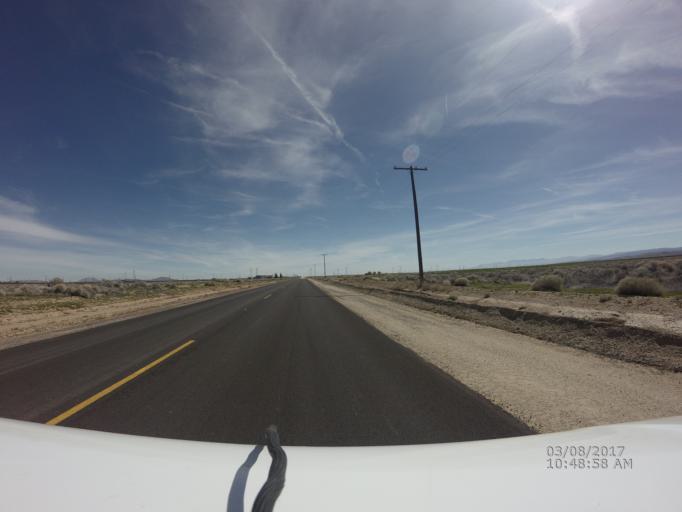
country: US
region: California
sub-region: Los Angeles County
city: Green Valley
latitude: 34.8188
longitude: -118.4274
